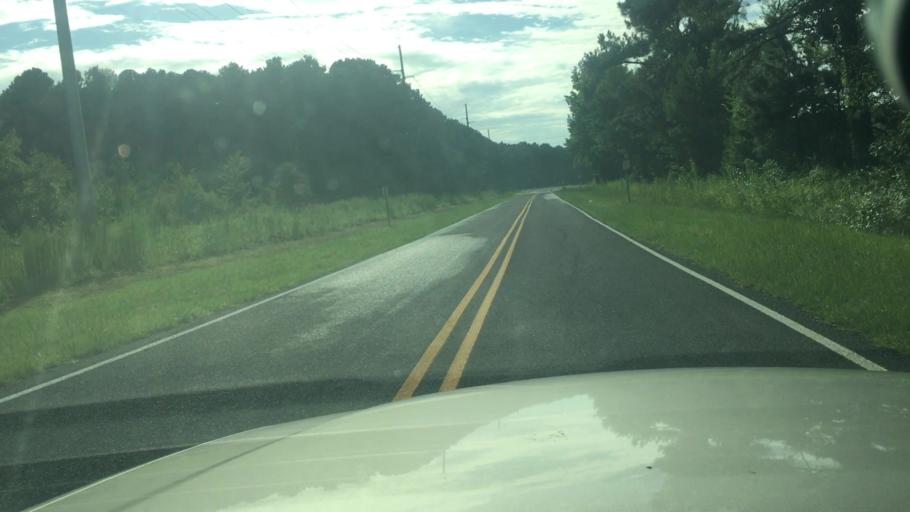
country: US
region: North Carolina
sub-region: Cumberland County
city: Eastover
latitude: 35.1642
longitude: -78.8537
